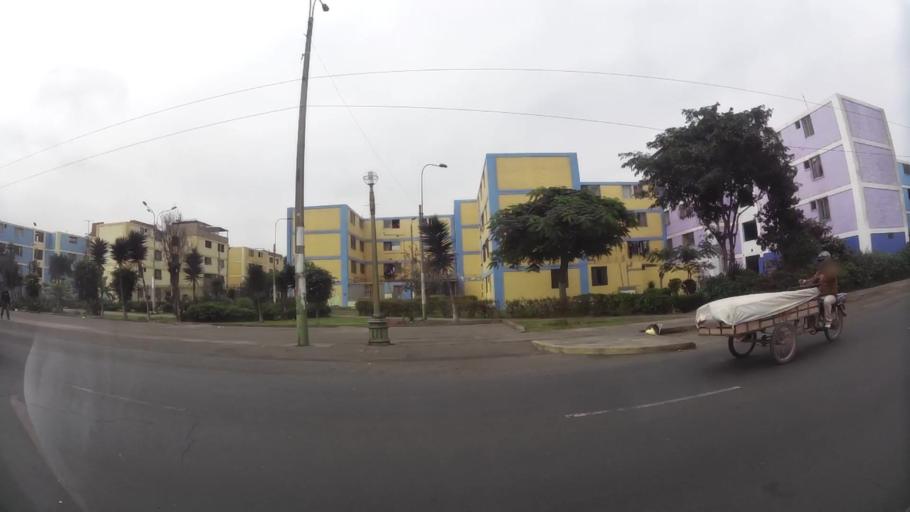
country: PE
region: Callao
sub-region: Callao
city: Callao
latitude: -12.0155
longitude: -77.1032
